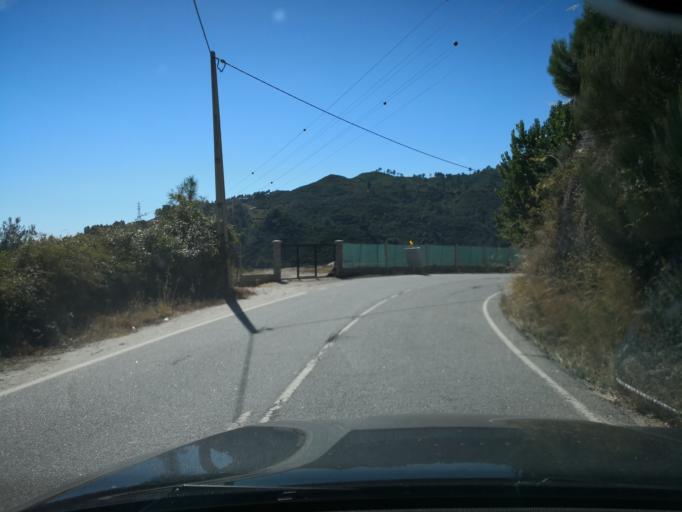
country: PT
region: Vila Real
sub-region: Vila Real
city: Vila Real
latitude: 41.2714
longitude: -7.7782
